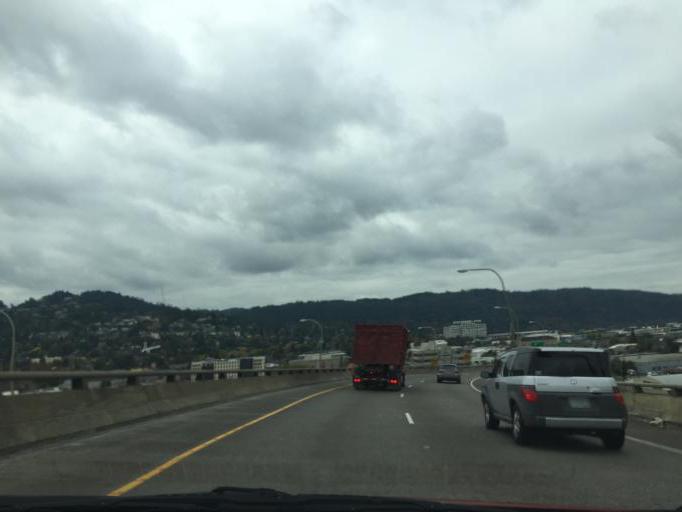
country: US
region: Oregon
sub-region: Multnomah County
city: Portland
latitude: 45.5348
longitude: -122.6879
